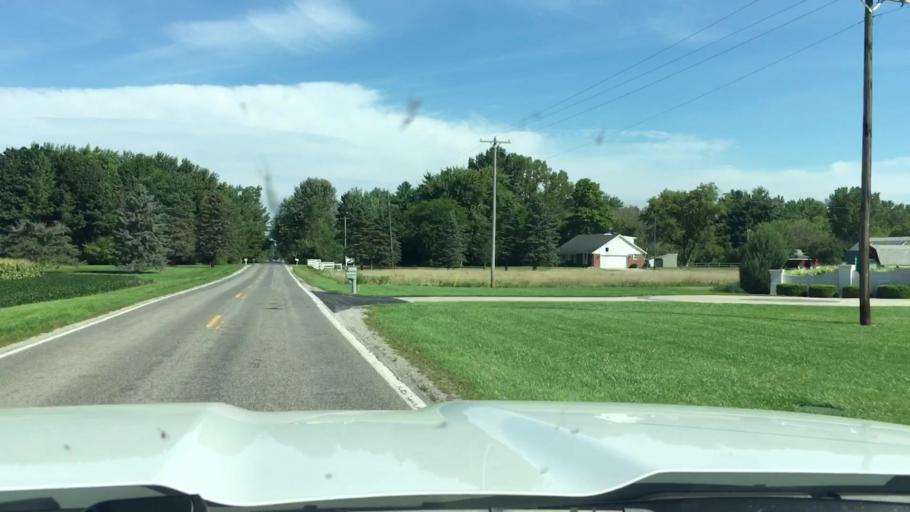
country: US
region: Michigan
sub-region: Saginaw County
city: Hemlock
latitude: 43.4702
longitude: -84.2303
